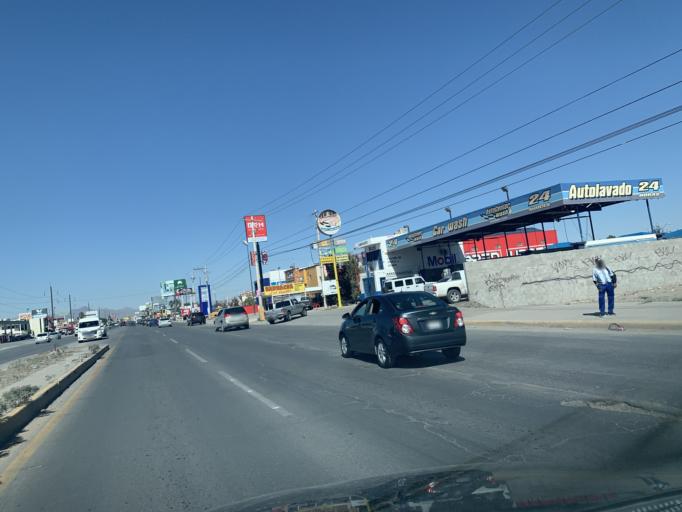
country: US
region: Texas
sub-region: El Paso County
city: Socorro
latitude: 31.6762
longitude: -106.3695
